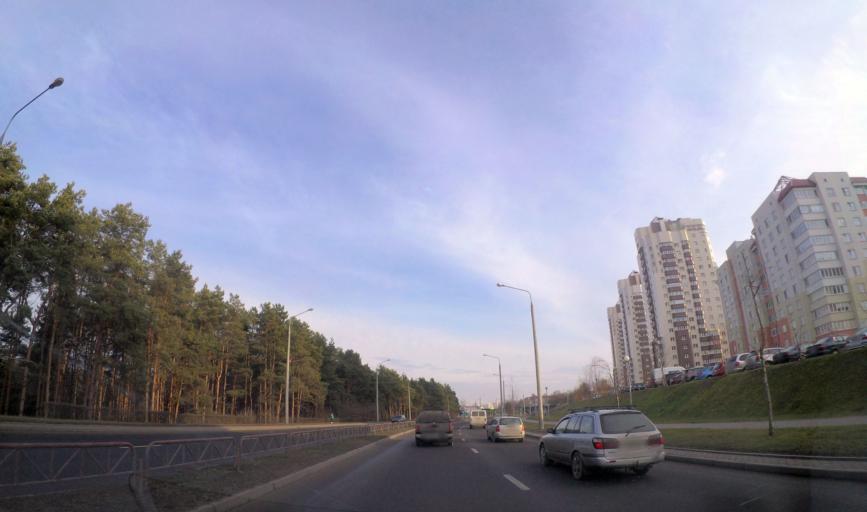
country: BY
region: Grodnenskaya
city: Hrodna
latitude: 53.6758
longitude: 23.7994
